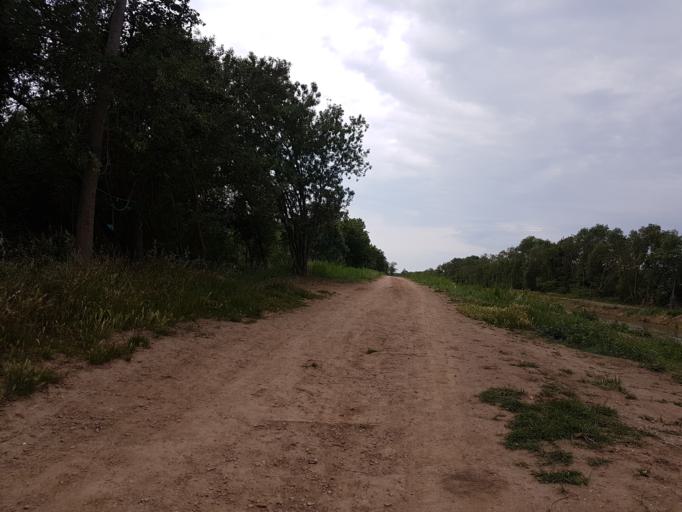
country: FR
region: Languedoc-Roussillon
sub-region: Departement de l'Herault
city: Agde
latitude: 43.3186
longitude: 3.4589
